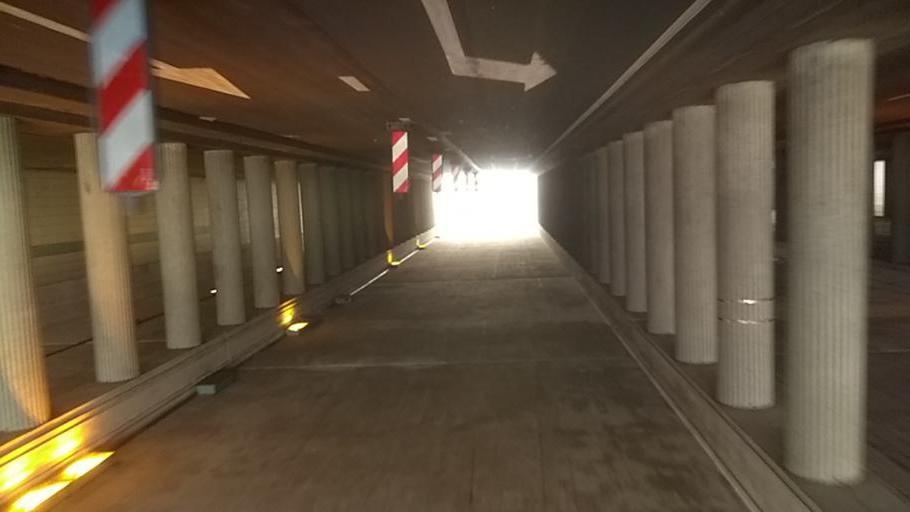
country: NL
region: Overijssel
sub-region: Gemeente Hengelo
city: Hengelo
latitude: 52.2621
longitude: 6.7923
